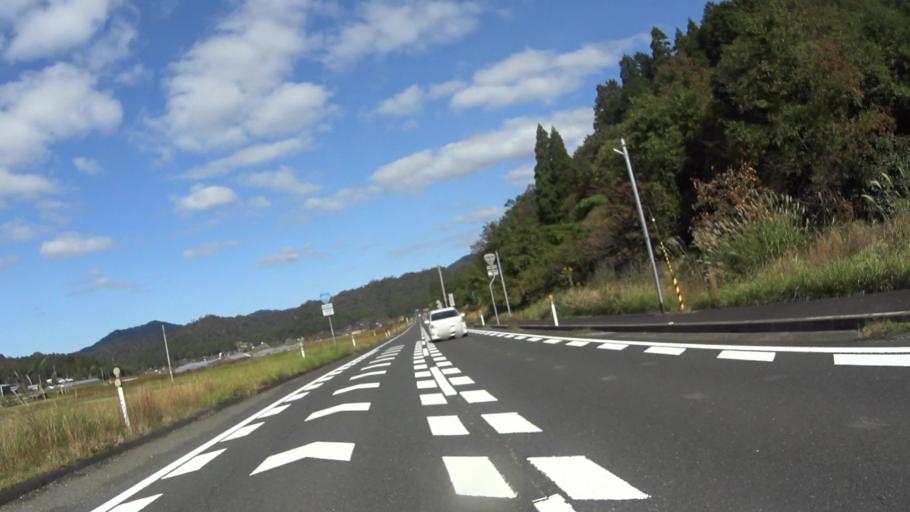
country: JP
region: Hyogo
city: Toyooka
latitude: 35.5670
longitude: 134.9737
